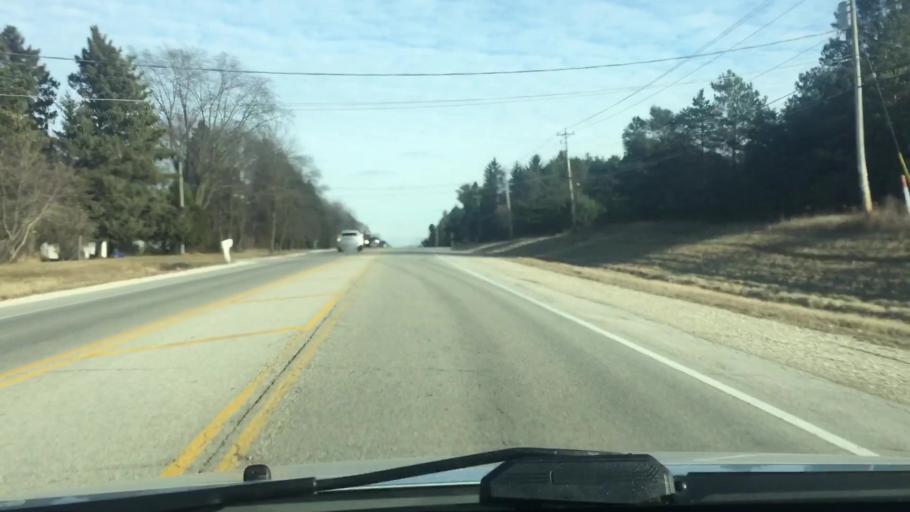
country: US
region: Wisconsin
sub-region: Waukesha County
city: Sussex
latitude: 43.1120
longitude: -88.2321
